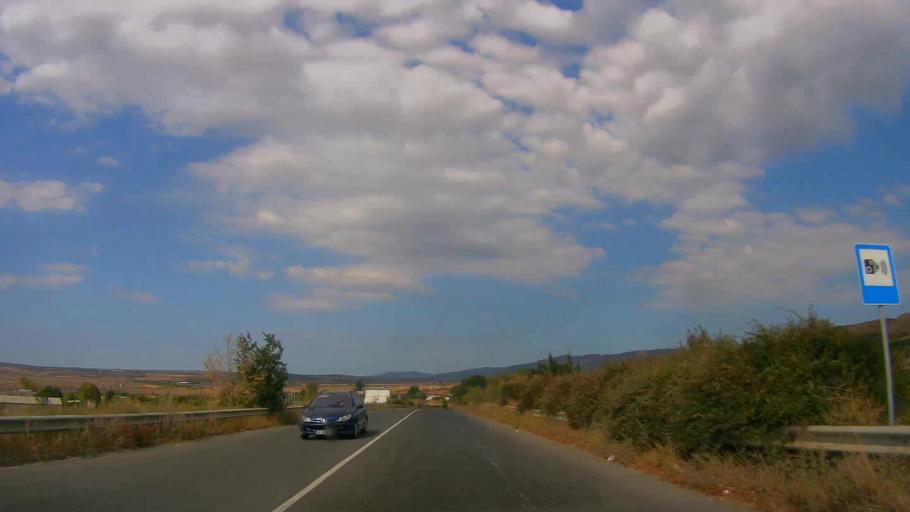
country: BG
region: Burgas
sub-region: Obshtina Aytos
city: Aytos
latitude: 42.7041
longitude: 27.2412
